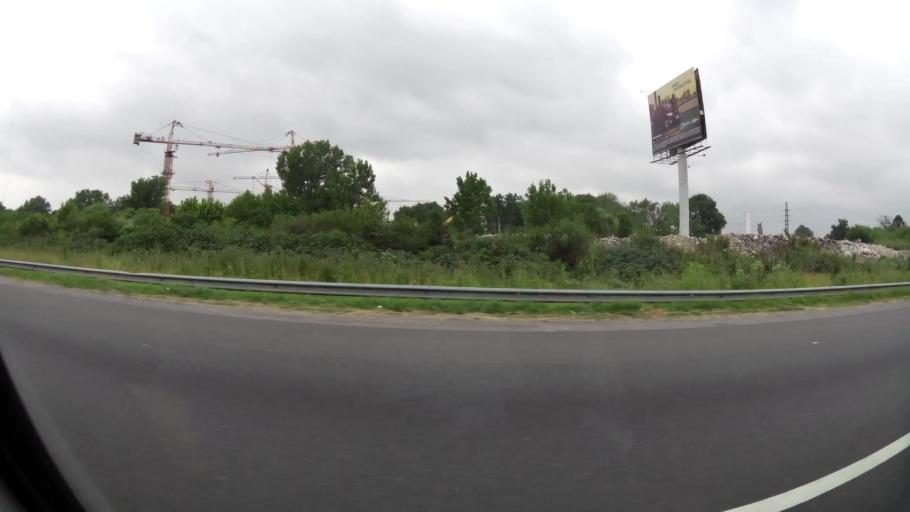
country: AR
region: Buenos Aires
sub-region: Partido de Avellaneda
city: Avellaneda
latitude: -34.6800
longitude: -58.3205
